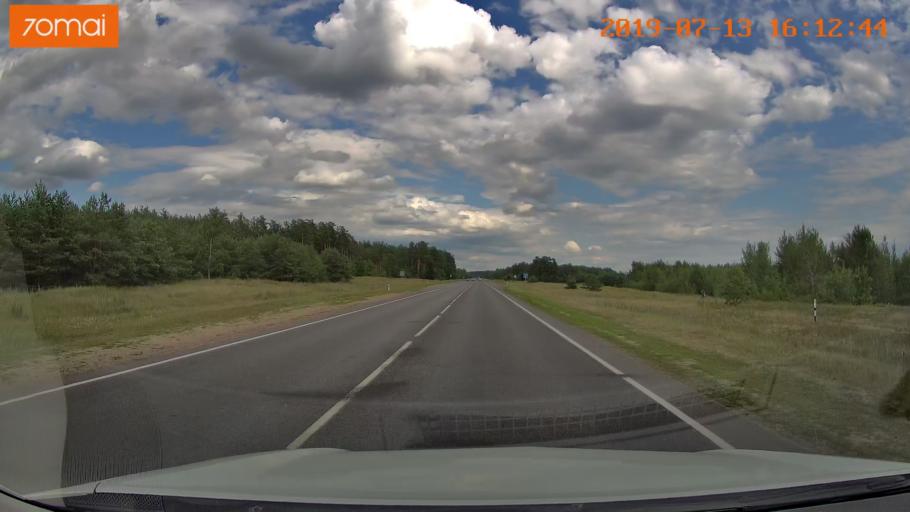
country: BY
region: Mogilev
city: Babruysk
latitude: 53.1658
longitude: 29.2870
